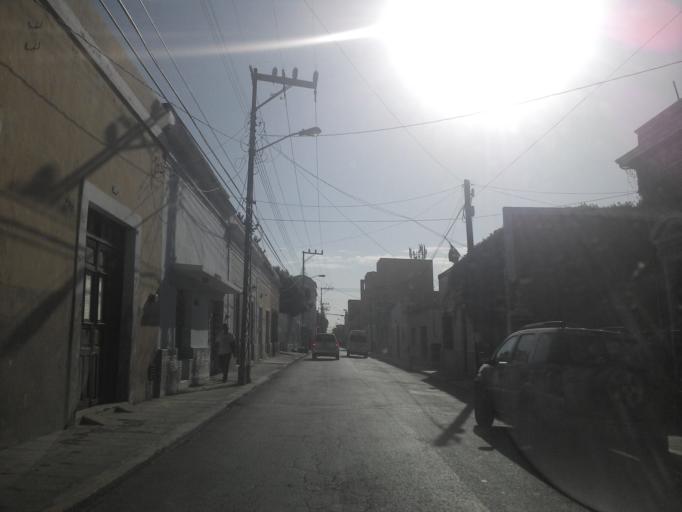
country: MX
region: Yucatan
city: Merida
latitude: 20.9676
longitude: -89.6306
